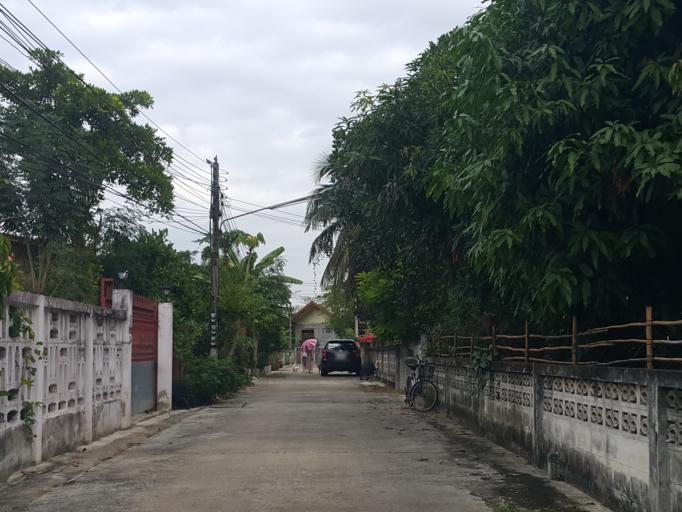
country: TH
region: Lampang
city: Lampang
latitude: 18.3072
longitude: 99.4971
